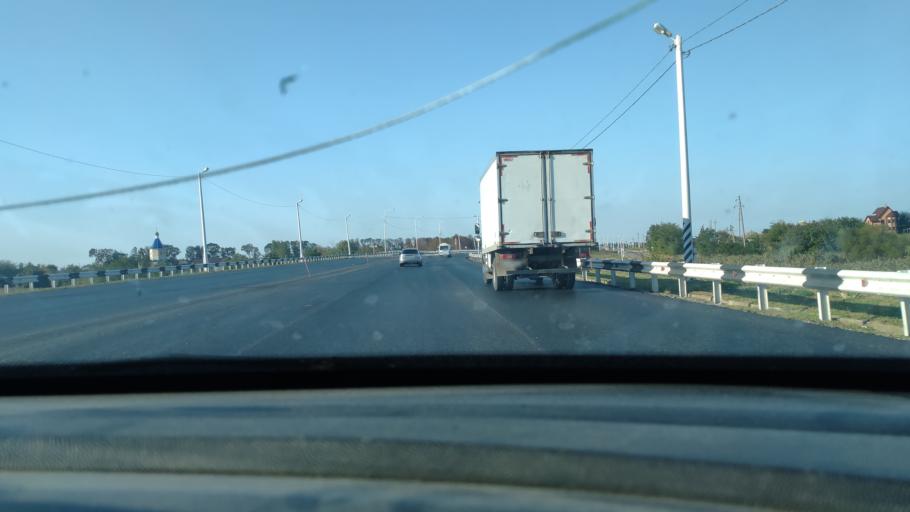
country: RU
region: Krasnodarskiy
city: Timashevsk
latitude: 45.5171
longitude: 38.9415
